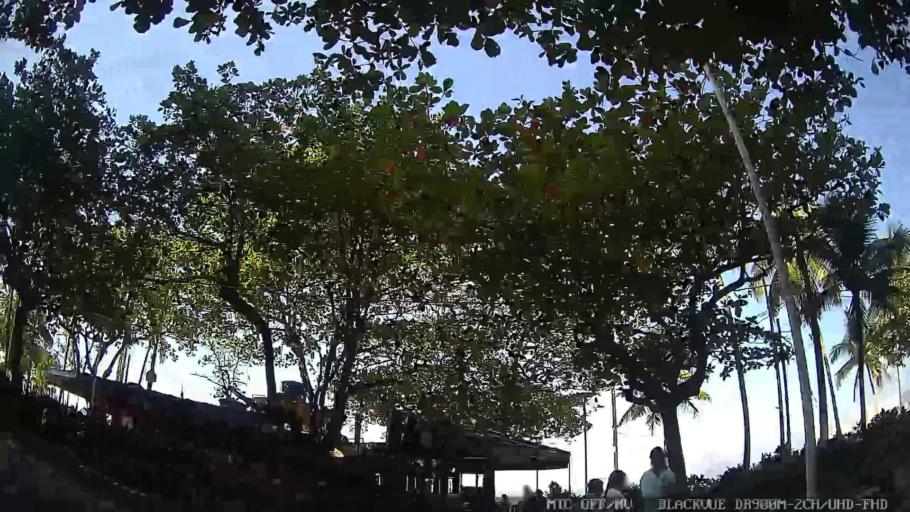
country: BR
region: Sao Paulo
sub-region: Guaruja
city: Guaruja
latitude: -23.9982
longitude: -46.2589
